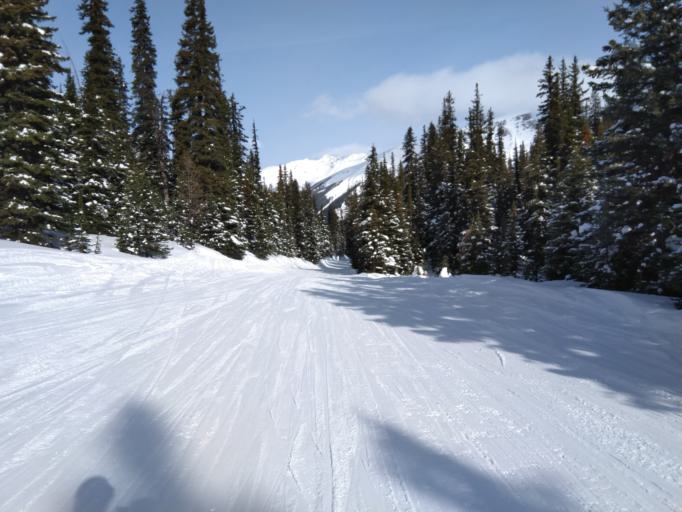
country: CA
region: Alberta
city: Banff
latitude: 51.0892
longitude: -115.7678
